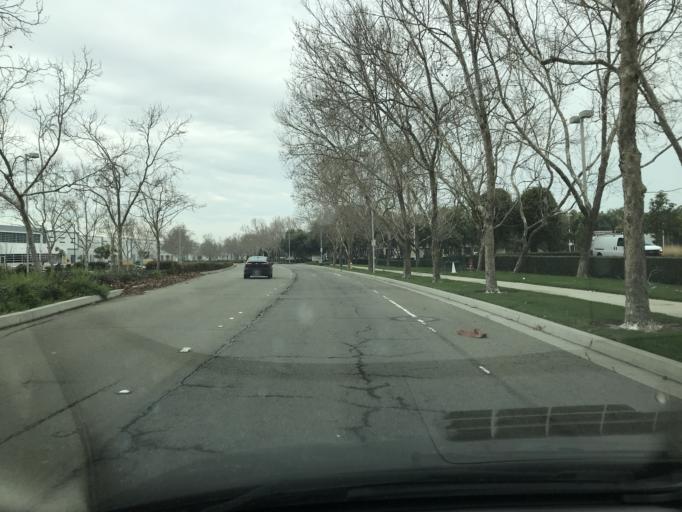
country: US
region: California
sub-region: Santa Clara County
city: Milpitas
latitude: 37.4338
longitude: -121.9222
